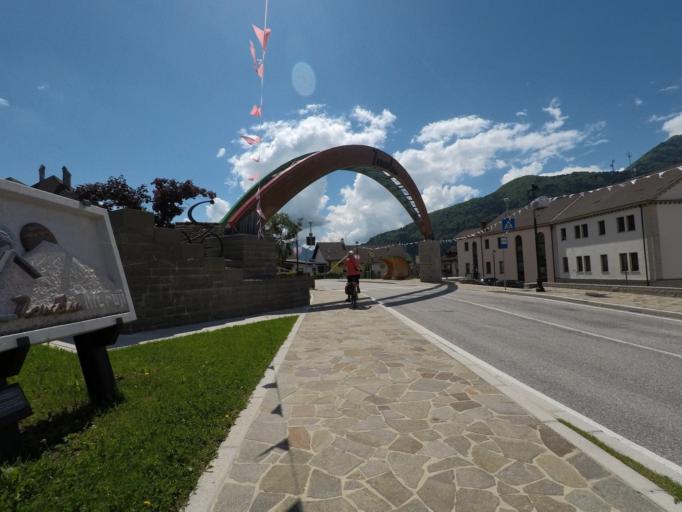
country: IT
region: Friuli Venezia Giulia
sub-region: Provincia di Udine
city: Ovaro
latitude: 46.4837
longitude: 12.8659
